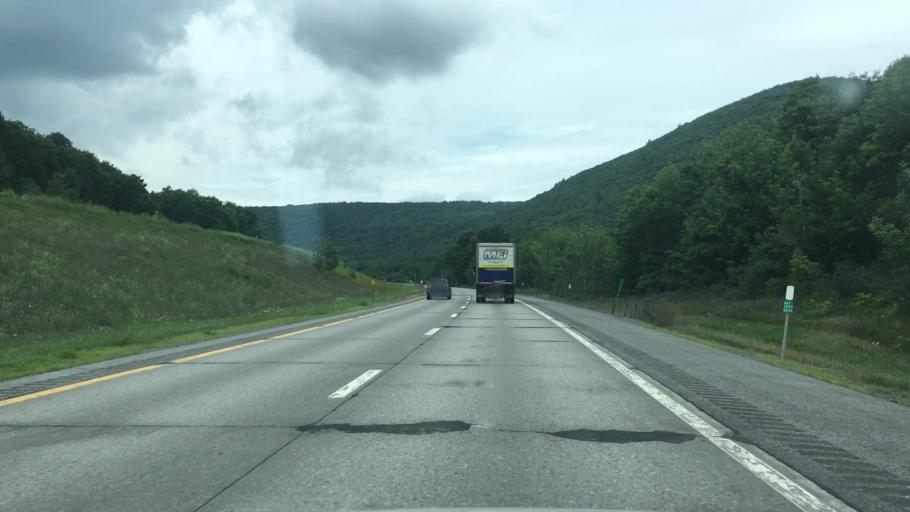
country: US
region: New York
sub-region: Otsego County
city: Worcester
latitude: 42.6502
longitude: -74.6285
